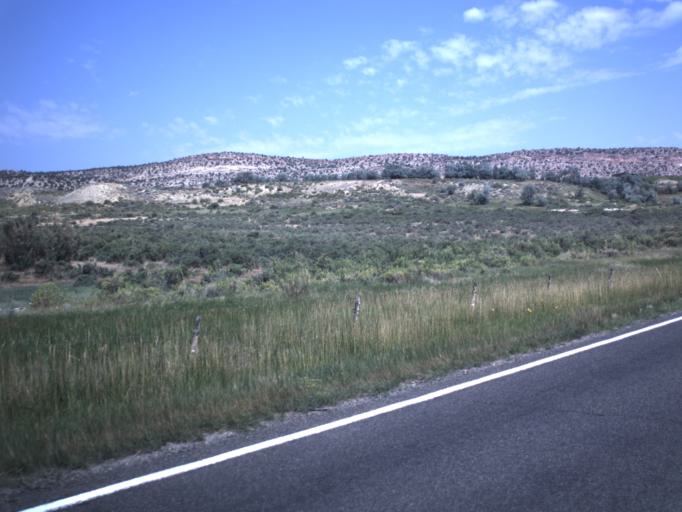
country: US
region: Utah
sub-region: Daggett County
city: Manila
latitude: 40.9778
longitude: -109.7226
